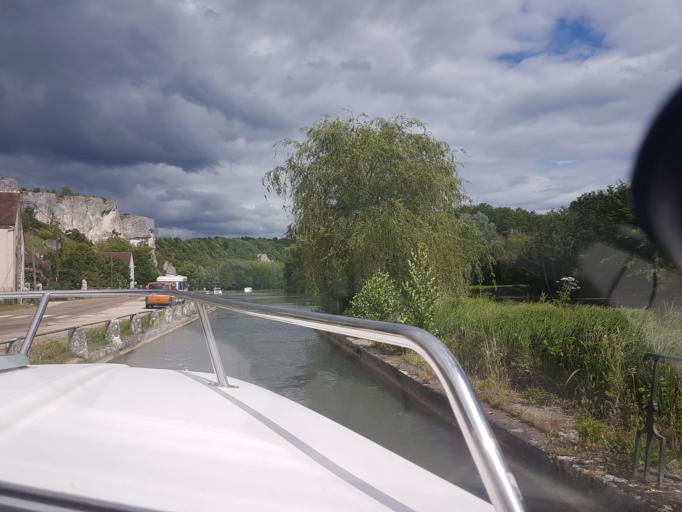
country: FR
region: Bourgogne
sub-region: Departement de l'Yonne
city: Vermenton
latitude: 47.5658
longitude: 3.6439
